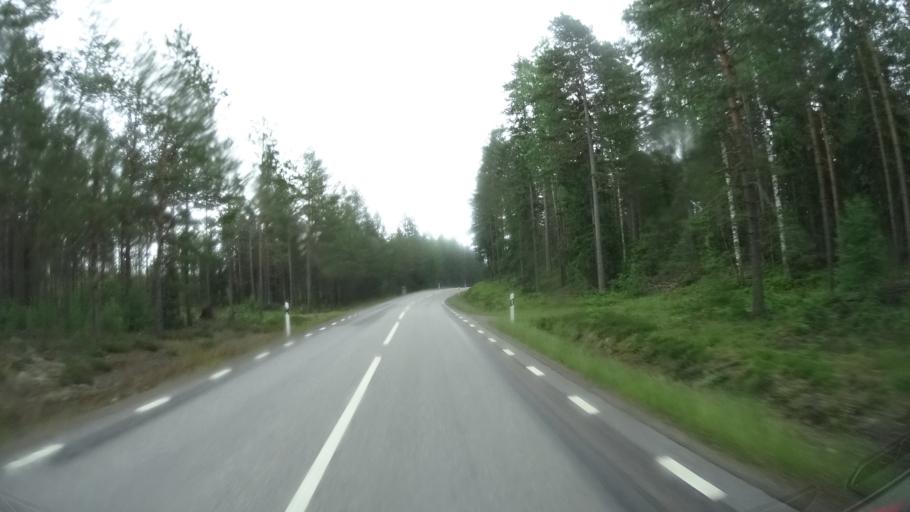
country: SE
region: Kalmar
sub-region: Hultsfreds Kommun
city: Hultsfred
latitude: 57.5289
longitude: 15.7853
